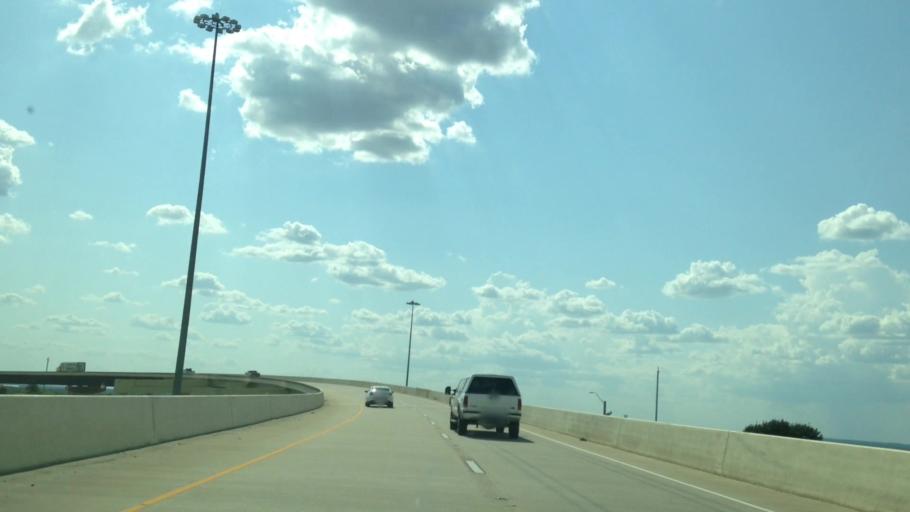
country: US
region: Texas
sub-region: Travis County
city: Onion Creek
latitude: 30.1122
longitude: -97.8041
